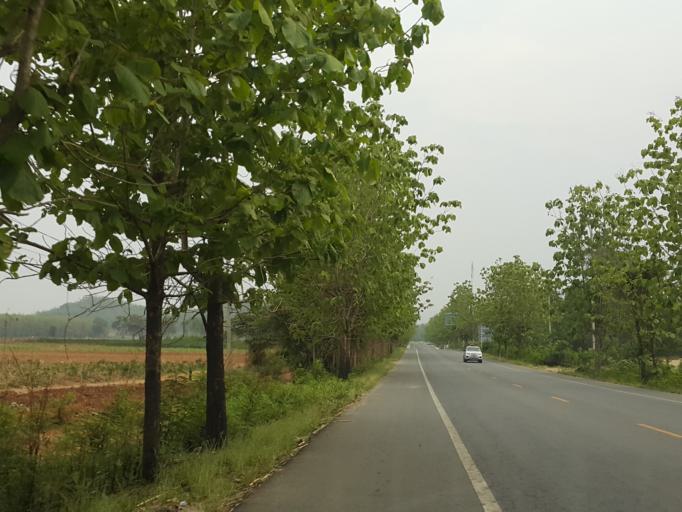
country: TH
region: Uthai Thani
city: Ban Rai
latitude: 15.0814
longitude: 99.5846
